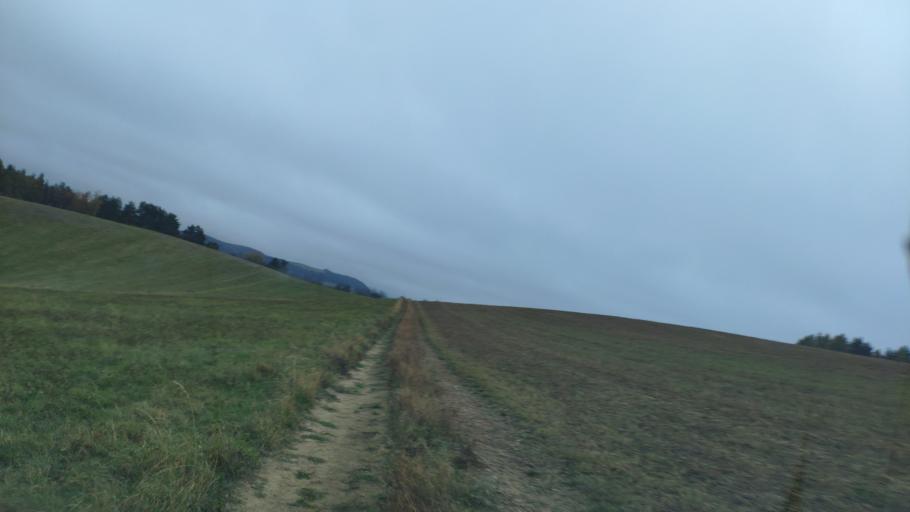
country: SK
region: Presovsky
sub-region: Okres Presov
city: Presov
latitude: 48.9319
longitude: 21.0916
